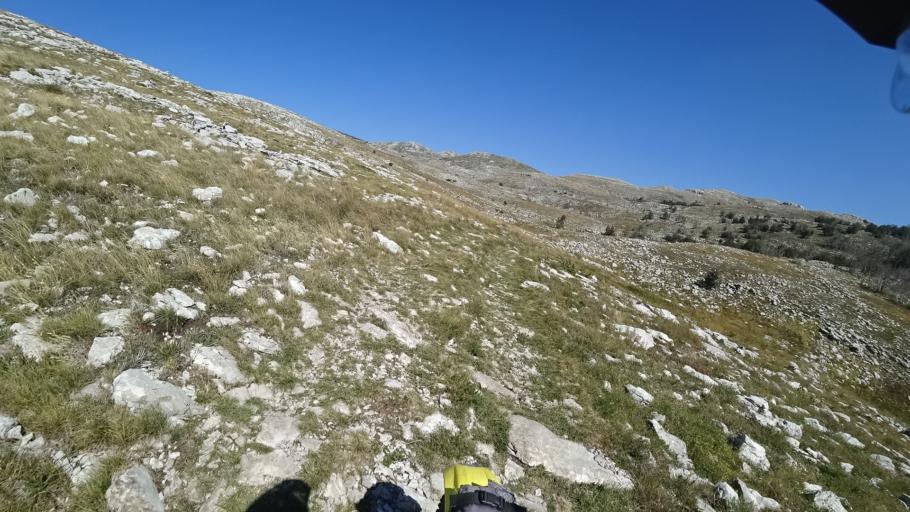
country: HR
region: Splitsko-Dalmatinska
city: Hrvace
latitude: 43.9180
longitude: 16.6051
